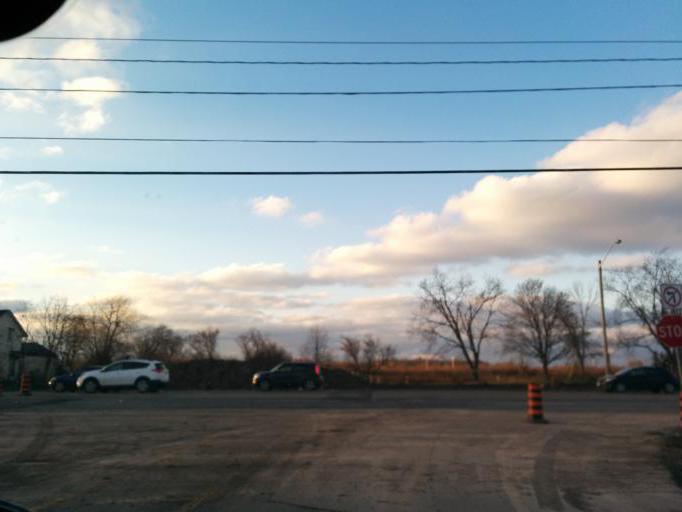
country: CA
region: Ontario
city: Burlington
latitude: 43.4380
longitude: -79.7736
